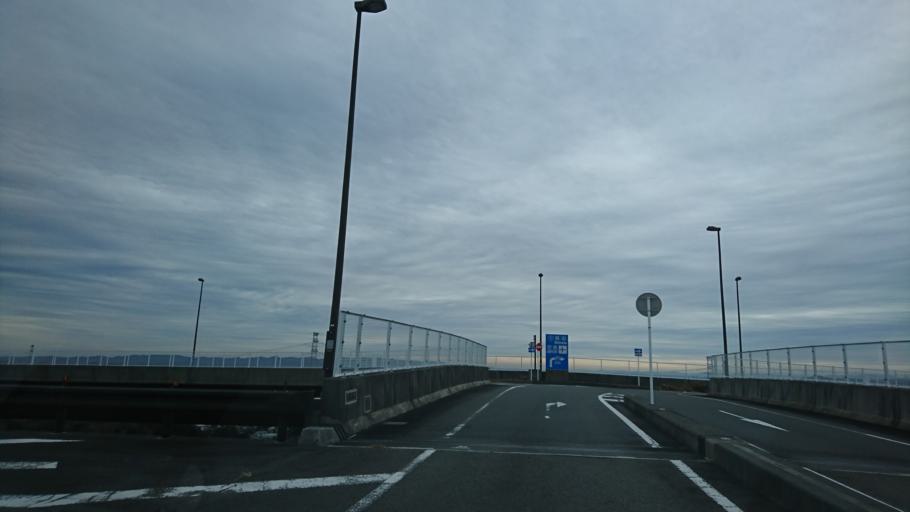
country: JP
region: Shizuoka
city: Kanaya
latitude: 34.7820
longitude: 138.1393
